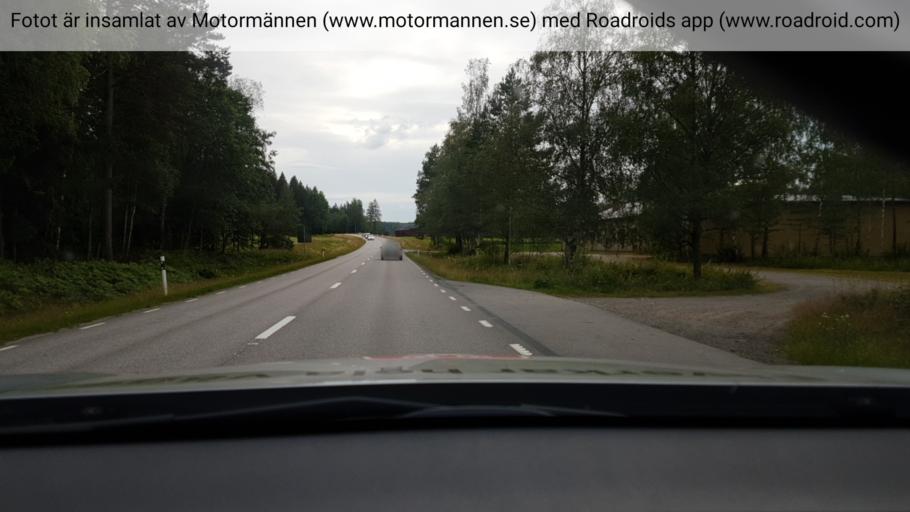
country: SE
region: Vaestra Goetaland
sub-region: Bengtsfors Kommun
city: Billingsfors
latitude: 58.9497
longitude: 12.2198
